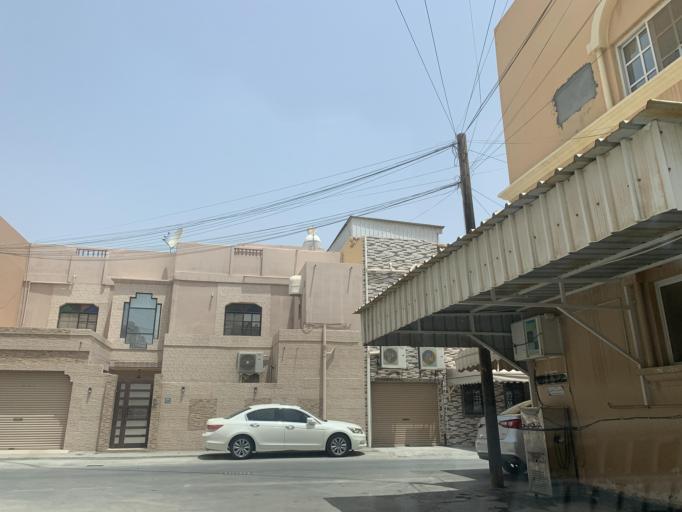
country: BH
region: Northern
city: Madinat `Isa
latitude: 26.1549
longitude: 50.5245
